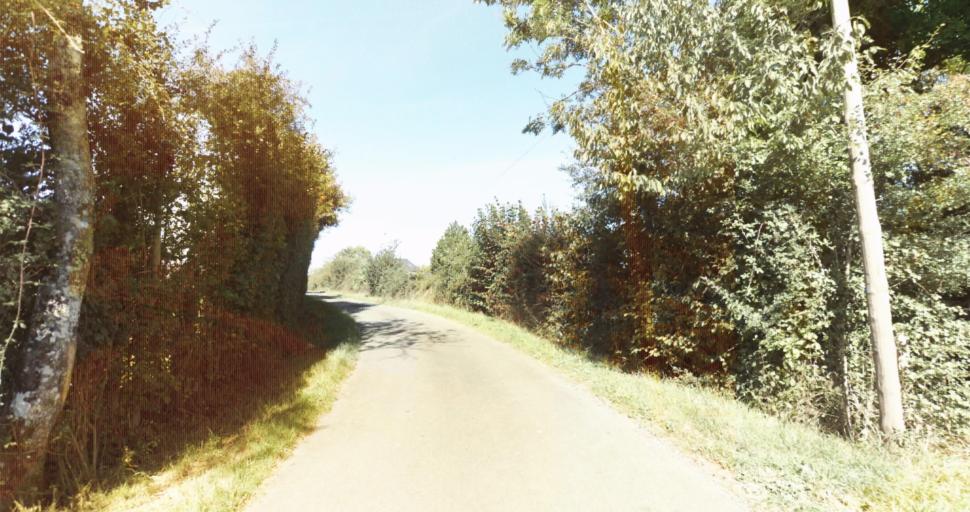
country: FR
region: Lower Normandy
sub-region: Departement de l'Orne
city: Gace
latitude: 48.7543
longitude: 0.2706
